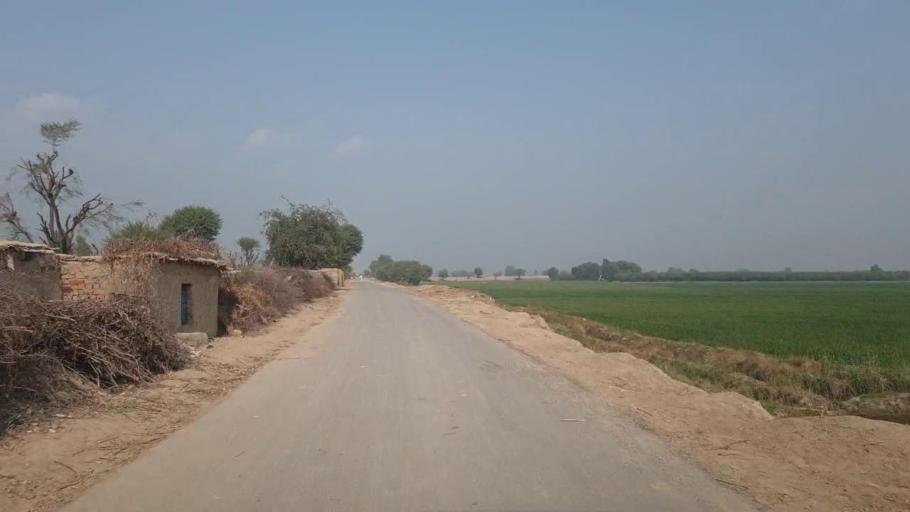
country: PK
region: Sindh
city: Hala
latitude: 25.7816
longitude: 68.3995
